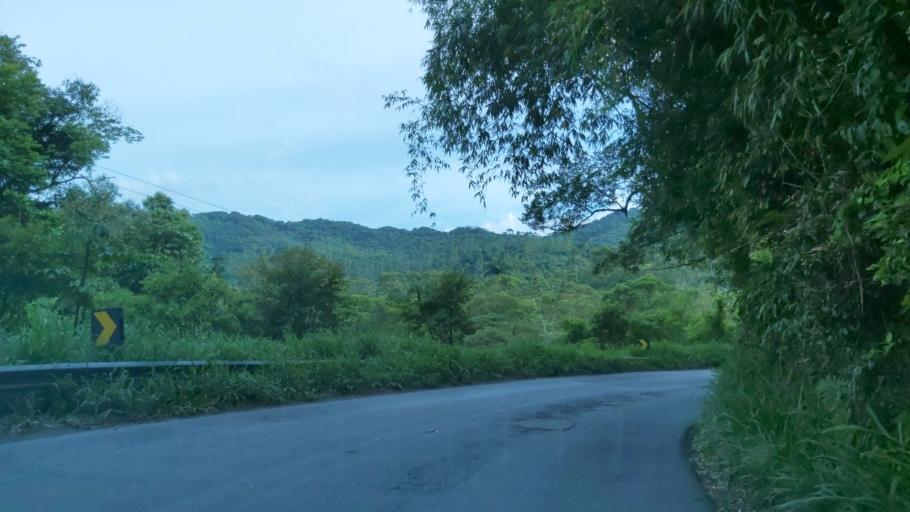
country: BR
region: Sao Paulo
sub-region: Juquia
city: Juquia
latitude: -24.0703
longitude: -47.6035
